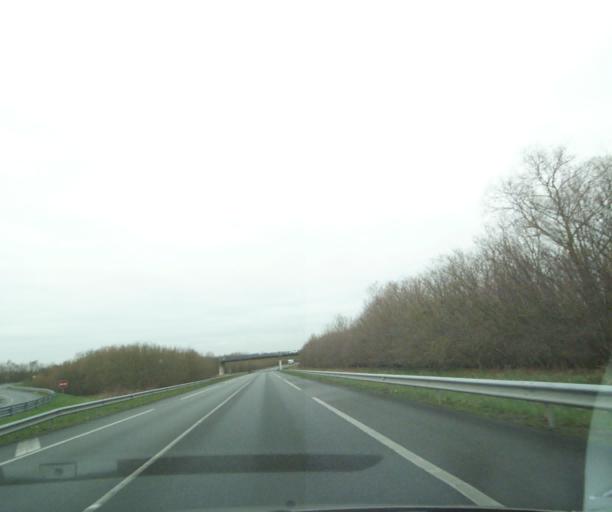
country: FR
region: Picardie
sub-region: Departement de l'Oise
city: Noyon
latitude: 49.5756
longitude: 3.0373
